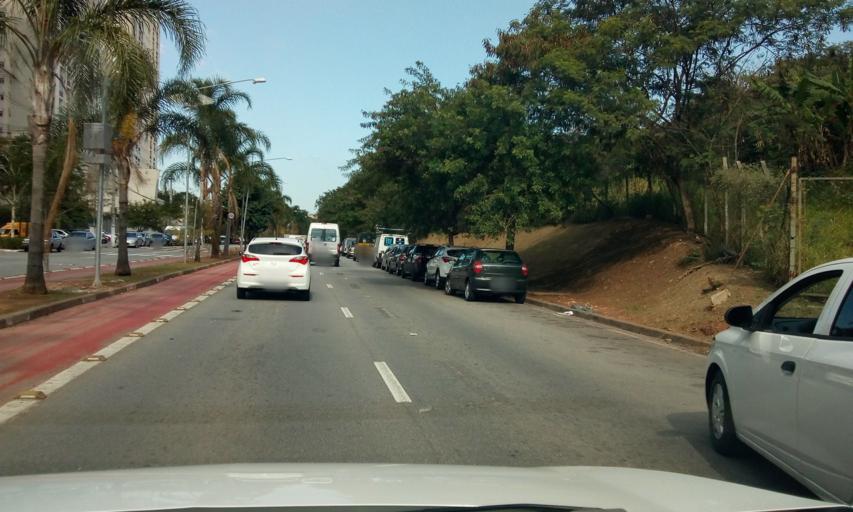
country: BR
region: Sao Paulo
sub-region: Osasco
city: Osasco
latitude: -23.5571
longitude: -46.7777
